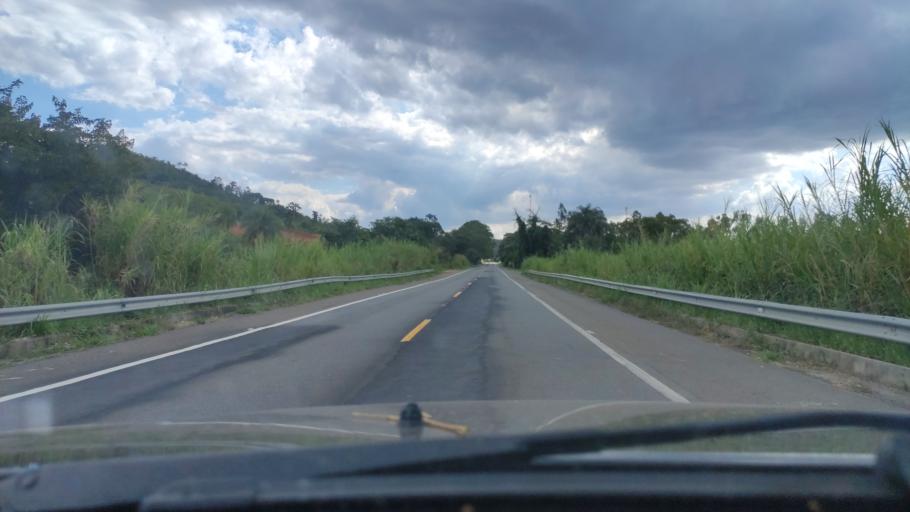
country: BR
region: Sao Paulo
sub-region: Itapira
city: Itapira
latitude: -22.4600
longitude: -46.7311
